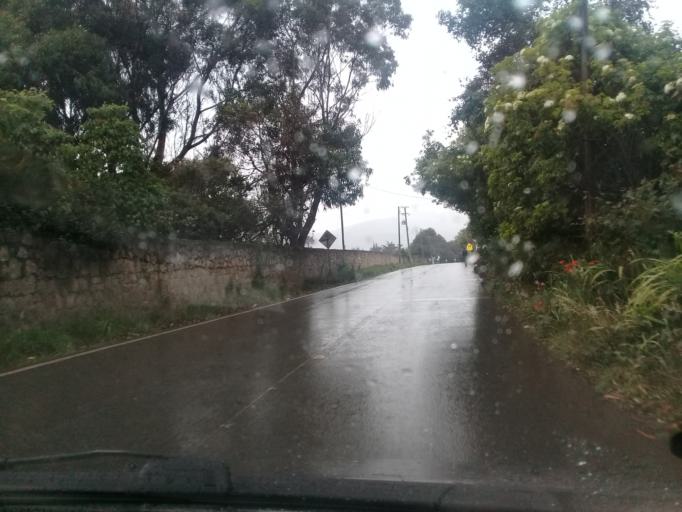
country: CO
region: Cundinamarca
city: Guasca
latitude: 4.8522
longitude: -73.8532
